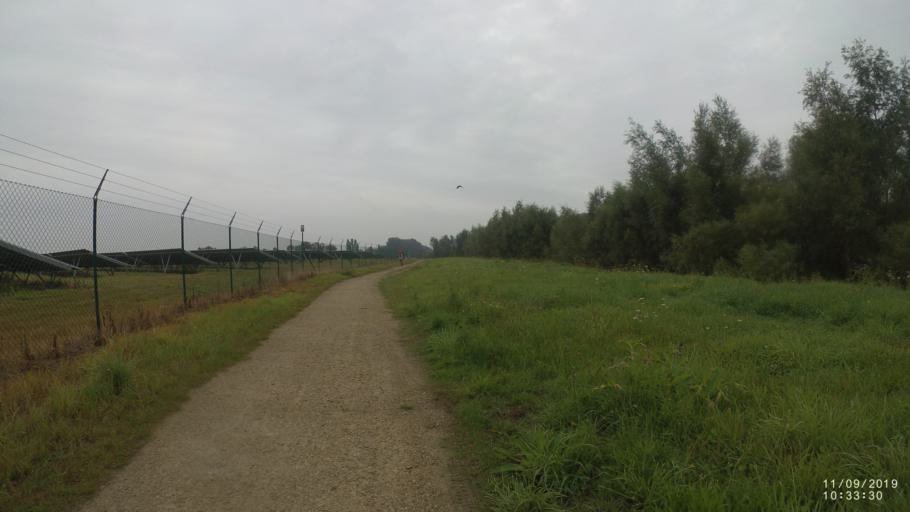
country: BE
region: Flanders
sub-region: Provincie Oost-Vlaanderen
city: Evergem
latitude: 51.0906
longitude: 3.6598
